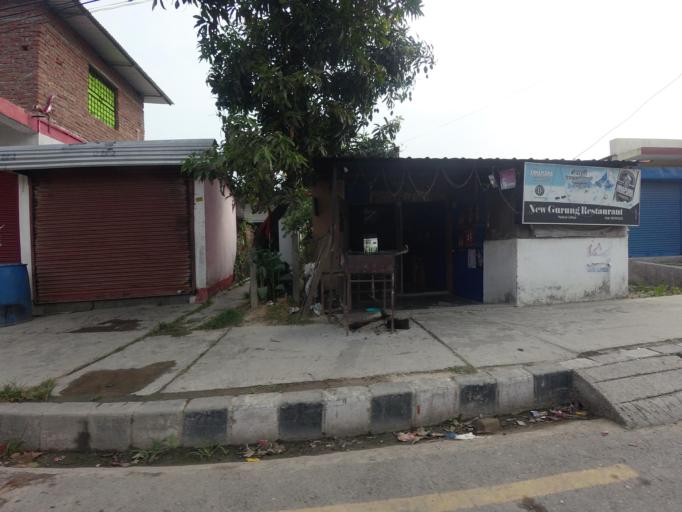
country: NP
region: Western Region
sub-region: Lumbini Zone
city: Bhairahawa
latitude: 27.4907
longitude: 83.4478
